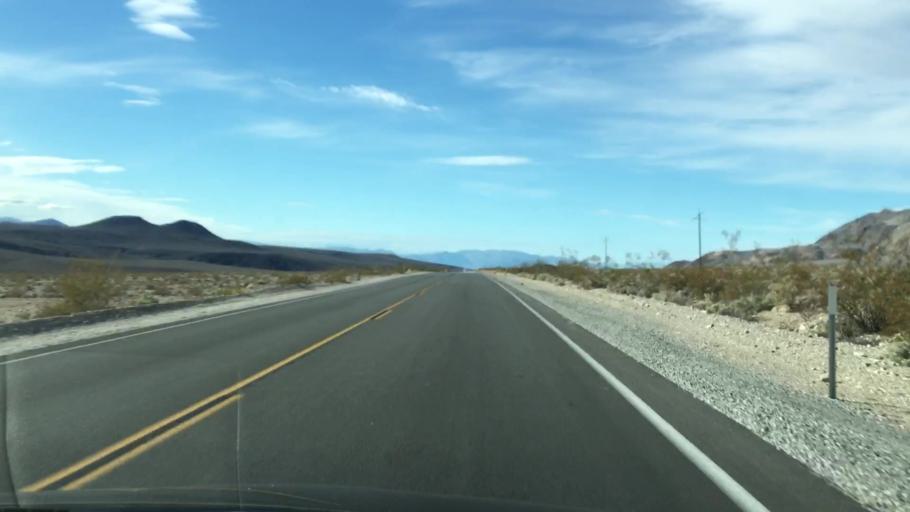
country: US
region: Nevada
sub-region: Nye County
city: Beatty
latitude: 36.3410
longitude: -116.5994
